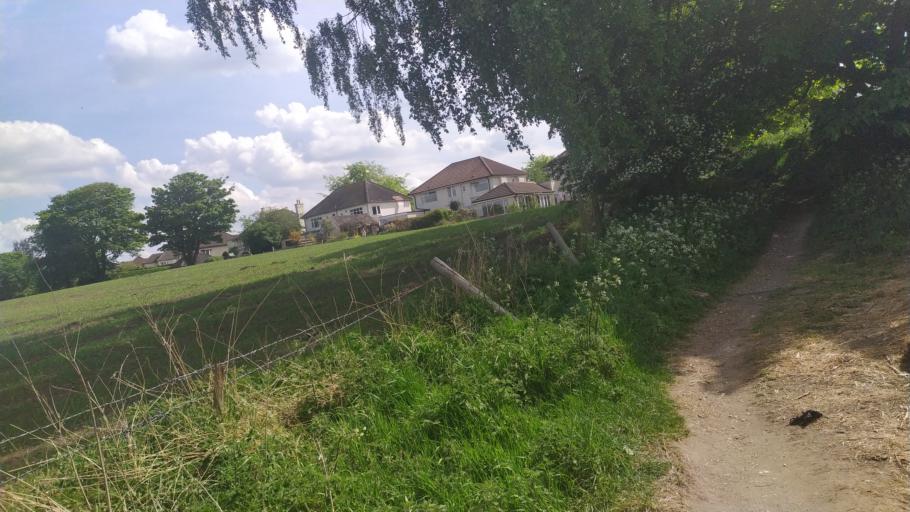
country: GB
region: England
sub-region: City and Borough of Leeds
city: Chapel Allerton
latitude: 53.8642
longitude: -1.5602
